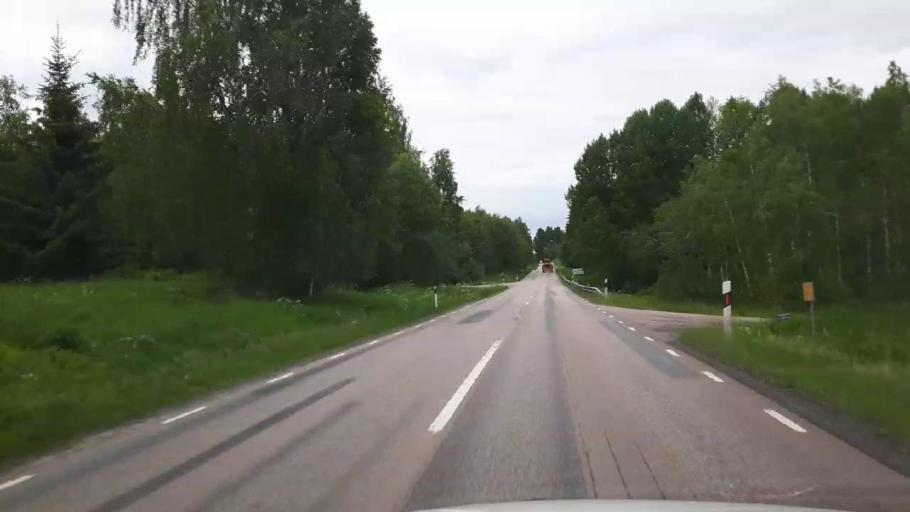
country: SE
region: Vaestmanland
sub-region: Kopings Kommun
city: Kolsva
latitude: 59.6129
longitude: 15.8270
